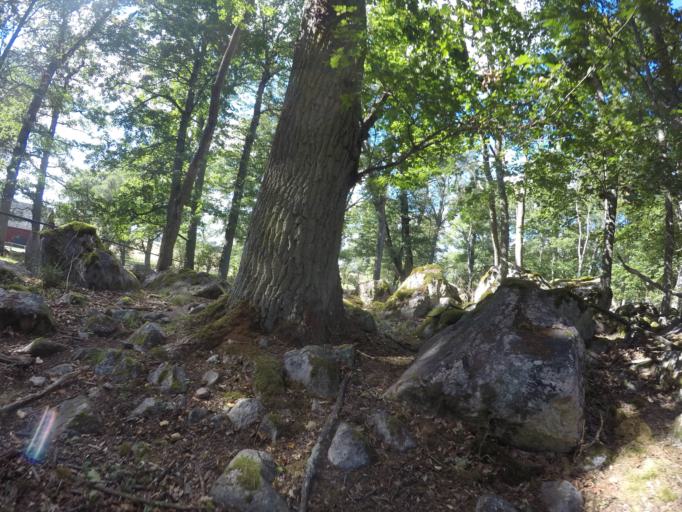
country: SE
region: Vaestmanland
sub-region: Hallstahammars Kommun
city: Kolback
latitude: 59.5020
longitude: 16.2300
